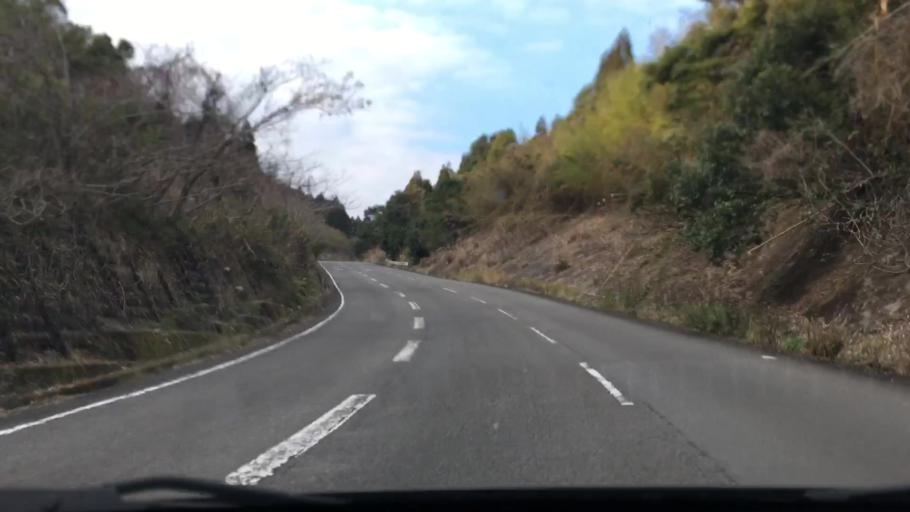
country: JP
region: Miyazaki
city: Nichinan
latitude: 31.6342
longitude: 131.3387
